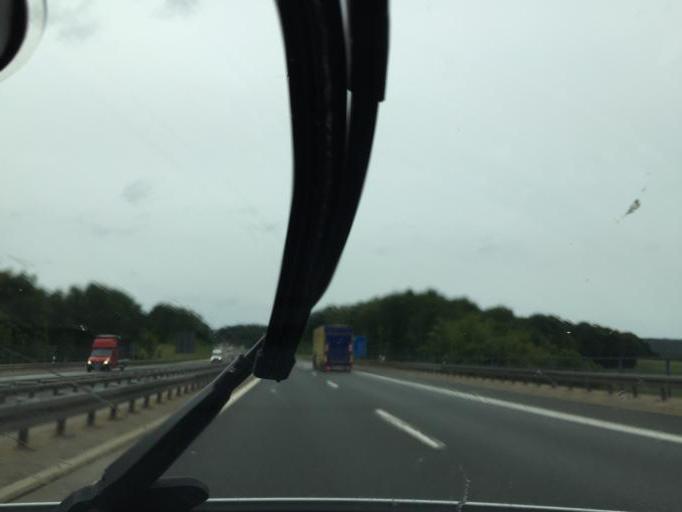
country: DE
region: Bavaria
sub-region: Regierungsbezirk Unterfranken
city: Oberthulba
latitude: 50.1906
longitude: 9.9434
